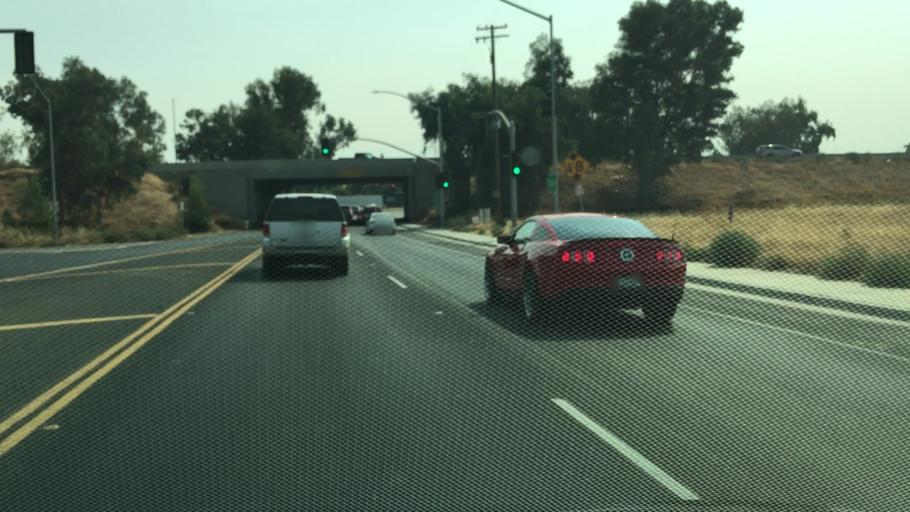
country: US
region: California
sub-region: Fresno County
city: Biola
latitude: 36.8330
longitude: -119.9168
